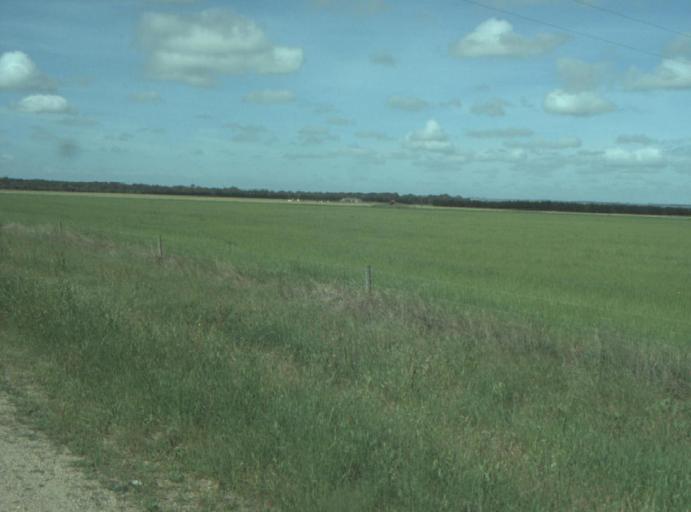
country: AU
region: Victoria
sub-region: Greater Geelong
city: Lara
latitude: -37.9855
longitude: 144.4219
